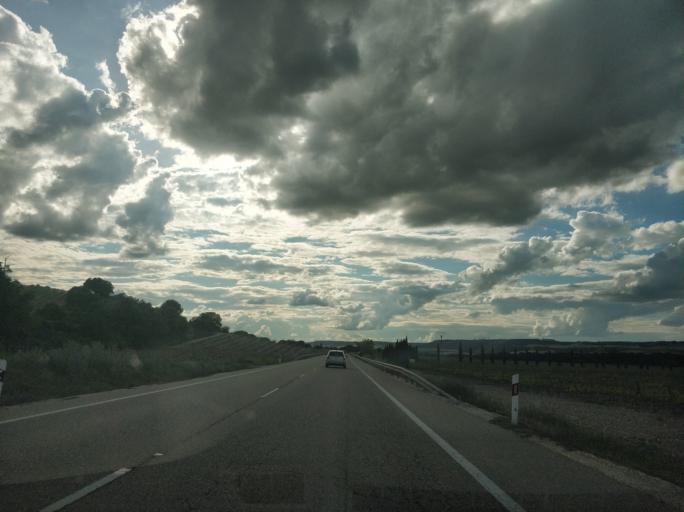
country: ES
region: Castille and Leon
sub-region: Provincia de Valladolid
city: Valbuena de Duero
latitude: 41.6259
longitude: -4.2779
